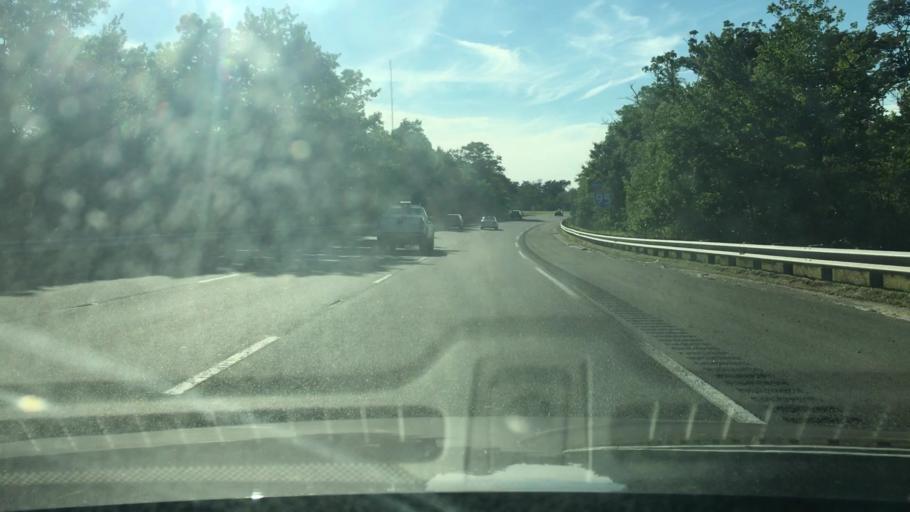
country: US
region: Massachusetts
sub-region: Essex County
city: South Peabody
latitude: 42.5288
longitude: -70.9758
